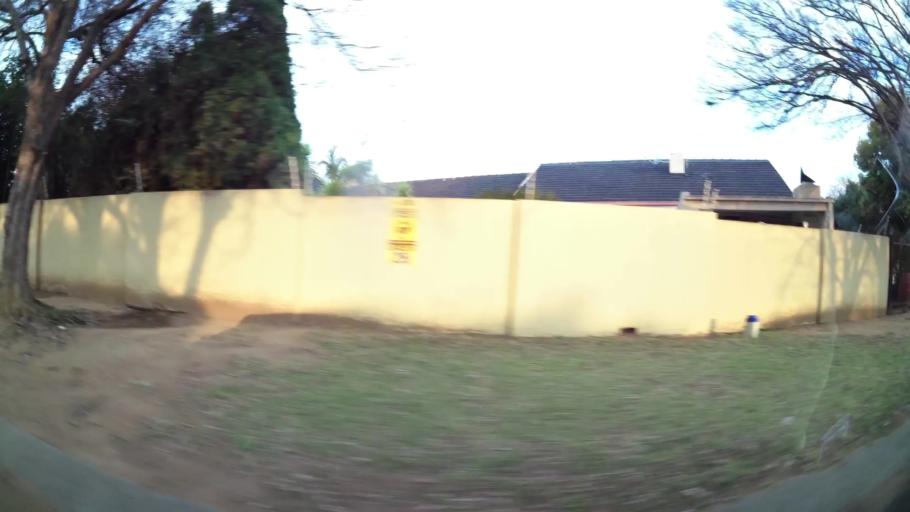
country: ZA
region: Gauteng
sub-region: Ekurhuleni Metropolitan Municipality
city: Benoni
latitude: -26.1530
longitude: 28.2959
